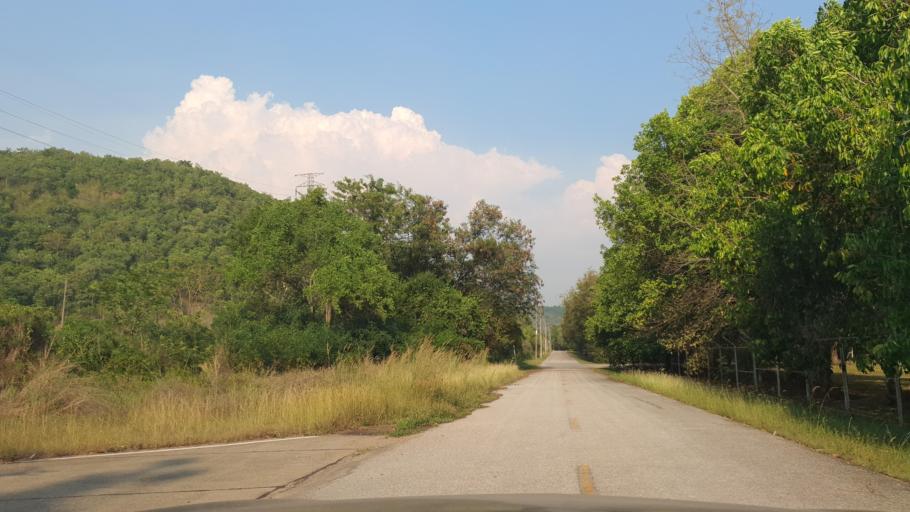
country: TH
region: Kanchanaburi
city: Sai Yok
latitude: 14.2255
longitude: 99.2250
